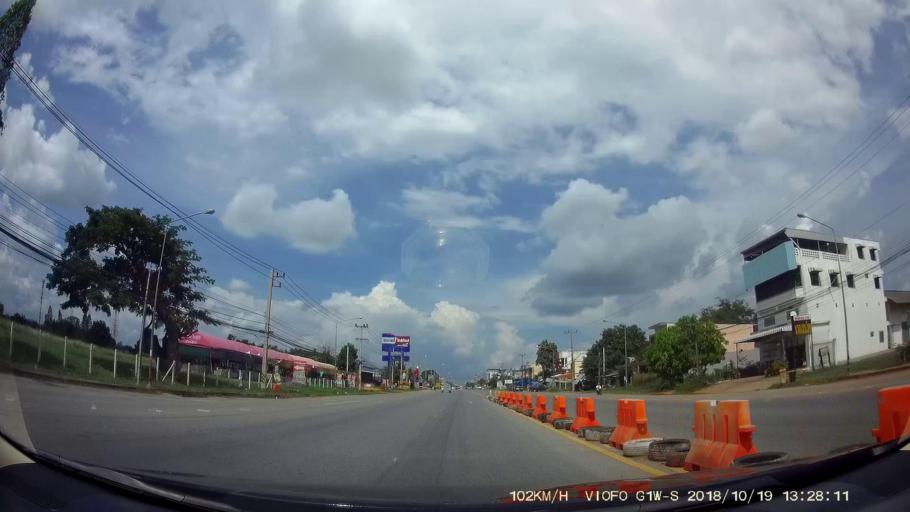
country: TH
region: Chaiyaphum
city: Chatturat
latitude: 15.5589
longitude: 101.8469
